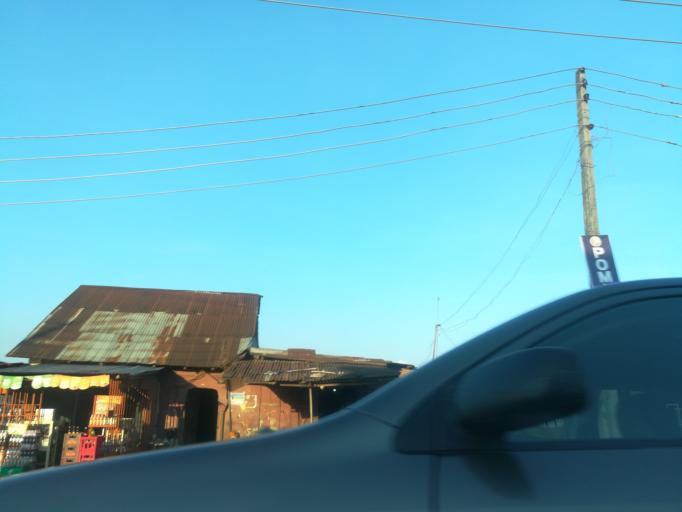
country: NG
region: Lagos
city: Ikorodu
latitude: 6.6159
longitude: 3.5097
